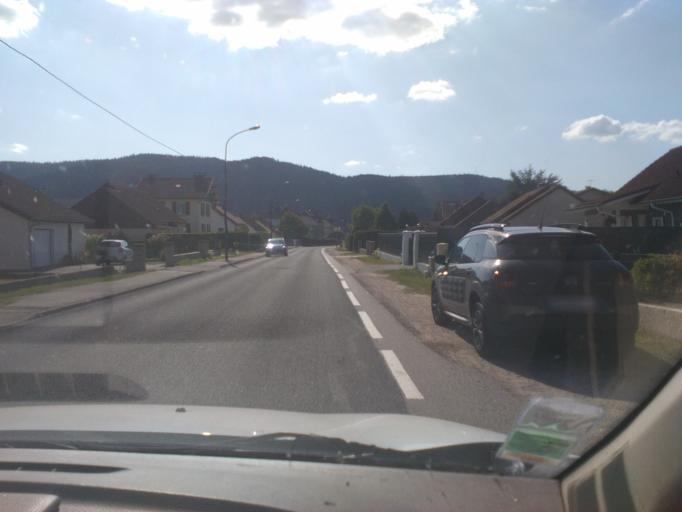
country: FR
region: Lorraine
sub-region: Departement des Vosges
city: Vagney
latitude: 48.0108
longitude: 6.7253
